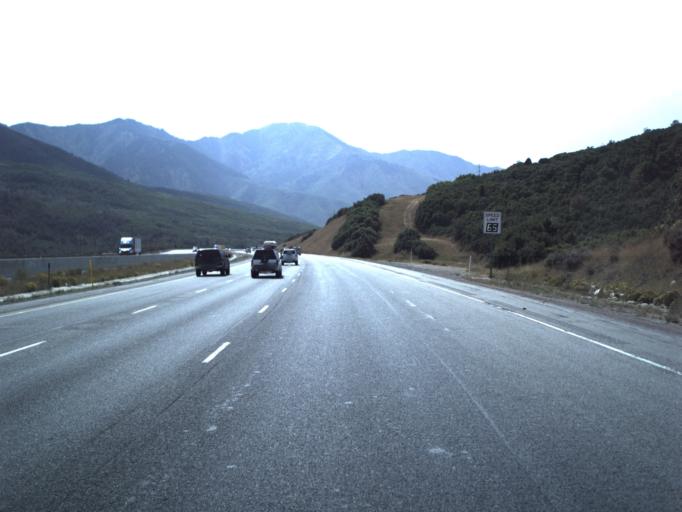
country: US
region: Utah
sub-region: Summit County
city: Summit Park
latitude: 40.7521
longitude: -111.6290
